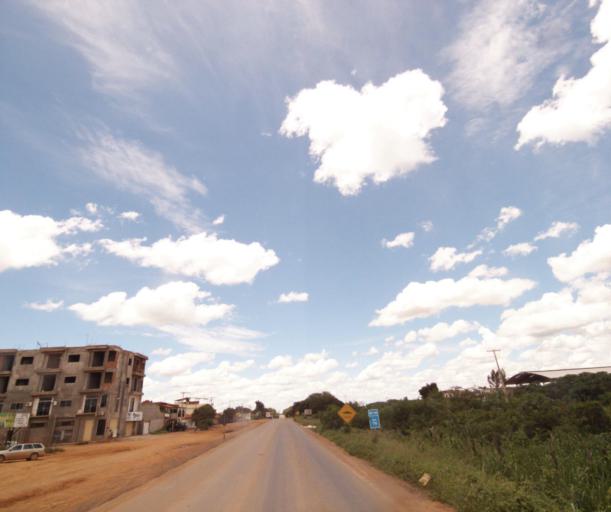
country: BR
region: Bahia
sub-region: Bom Jesus Da Lapa
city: Bom Jesus da Lapa
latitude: -13.2659
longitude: -43.5979
